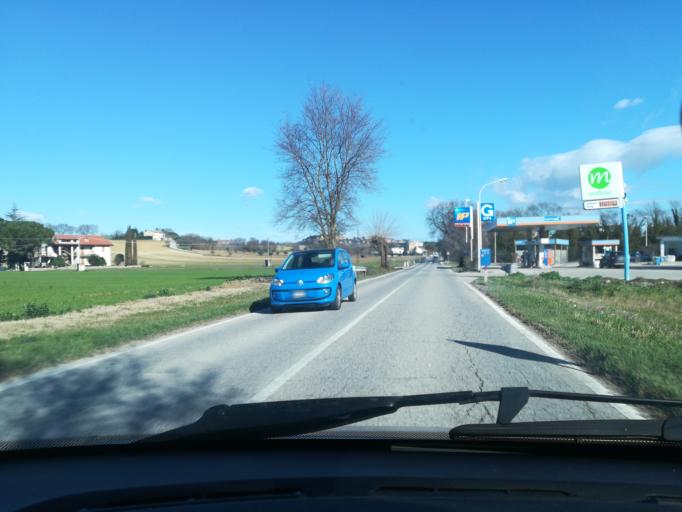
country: IT
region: The Marches
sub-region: Provincia di Macerata
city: Villa Potenza
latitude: 43.3377
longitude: 13.4290
